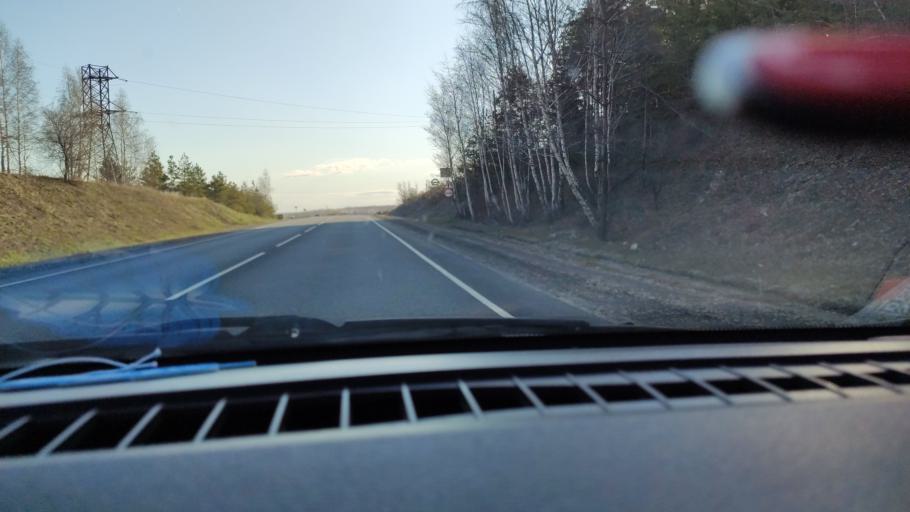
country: RU
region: Saratov
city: Khvalynsk
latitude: 52.5428
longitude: 48.0611
